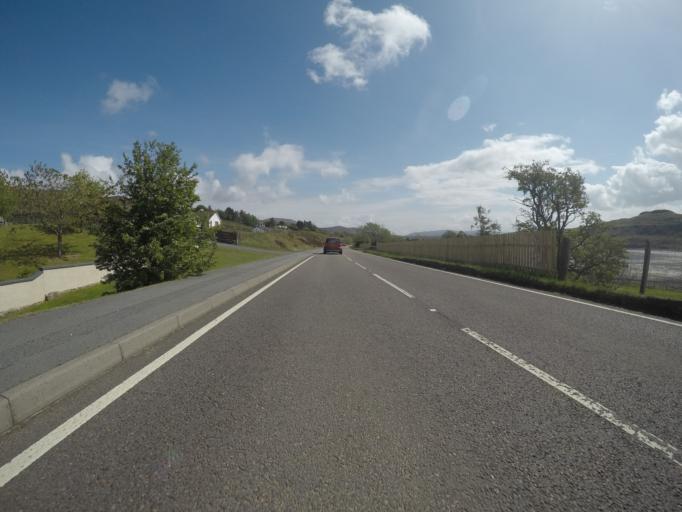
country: GB
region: Scotland
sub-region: Highland
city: Portree
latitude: 57.4889
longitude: -6.3137
